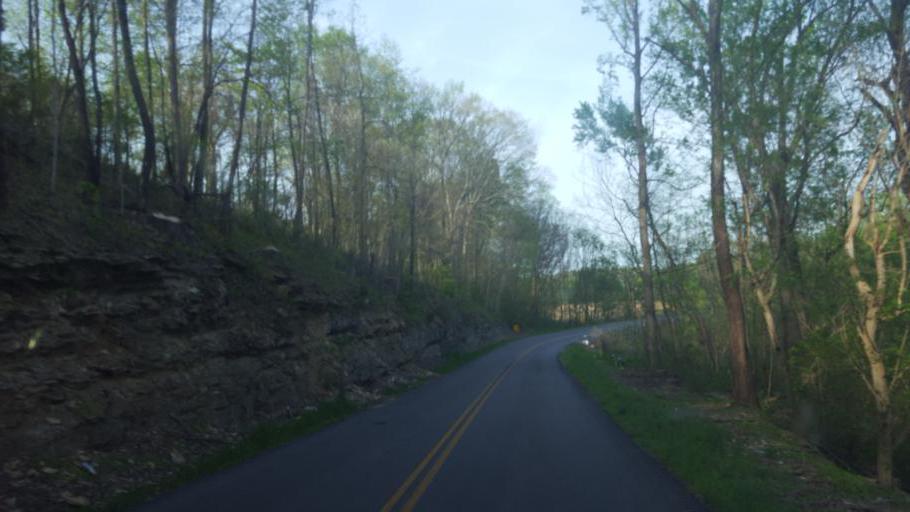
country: US
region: Kentucky
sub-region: Allen County
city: Scottsville
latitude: 36.8886
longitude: -86.1483
